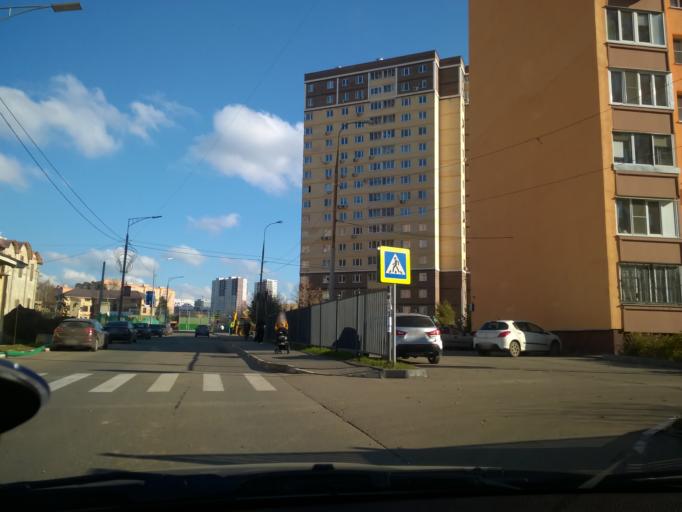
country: RU
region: Moskovskaya
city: Kommunarka
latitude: 55.5696
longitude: 37.4738
